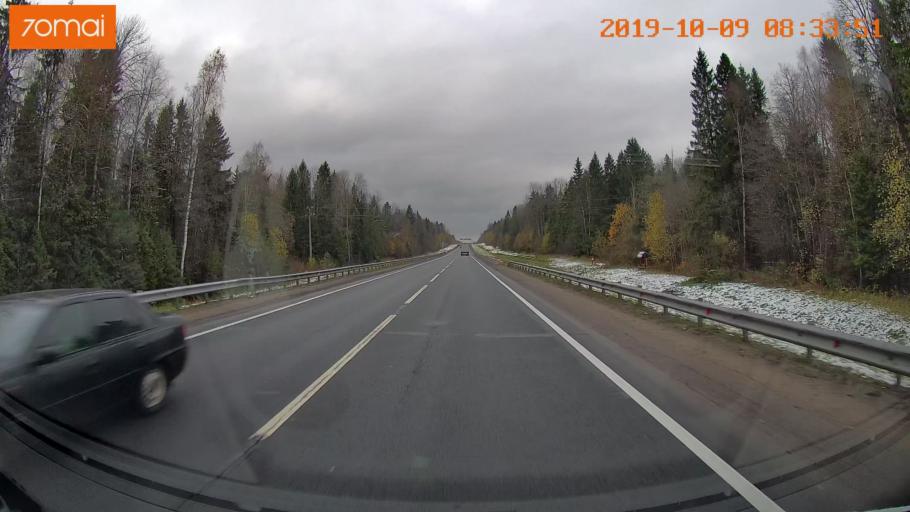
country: RU
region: Vologda
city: Gryazovets
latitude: 58.8882
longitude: 40.1896
